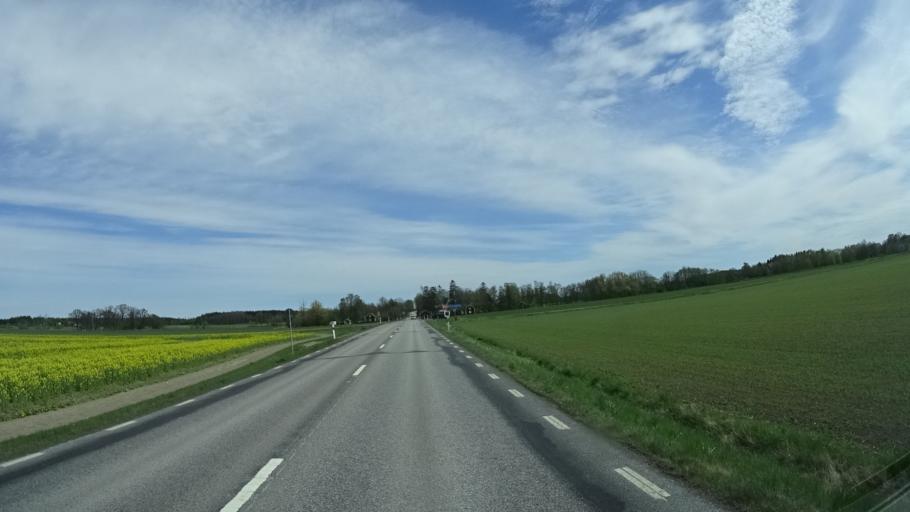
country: SE
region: OEstergoetland
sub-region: Linkopings Kommun
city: Vikingstad
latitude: 58.3704
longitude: 15.3669
